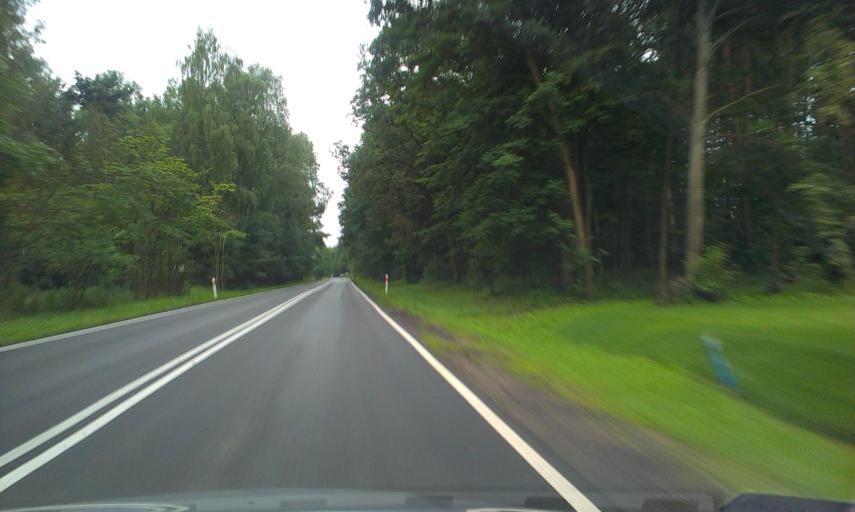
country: PL
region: Greater Poland Voivodeship
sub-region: Powiat pilski
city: Pila
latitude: 53.2342
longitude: 16.7914
